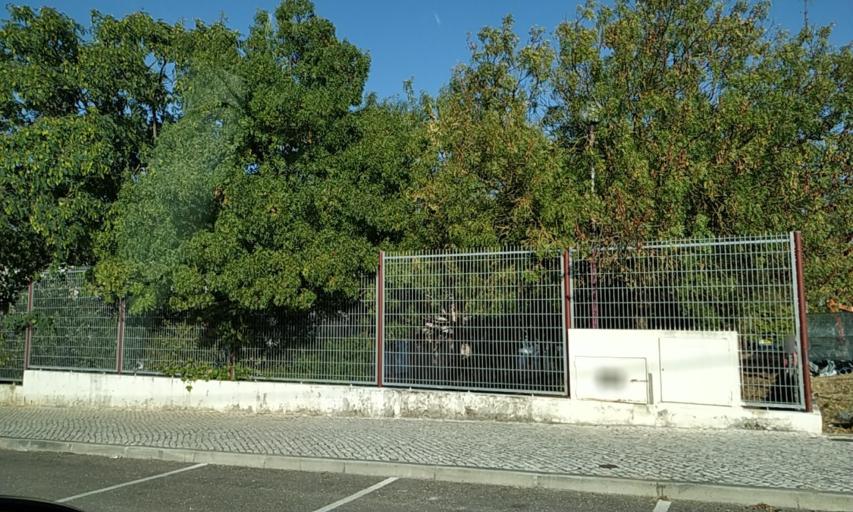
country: PT
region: Santarem
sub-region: Santarem
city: Santarem
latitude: 39.2513
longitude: -8.6842
